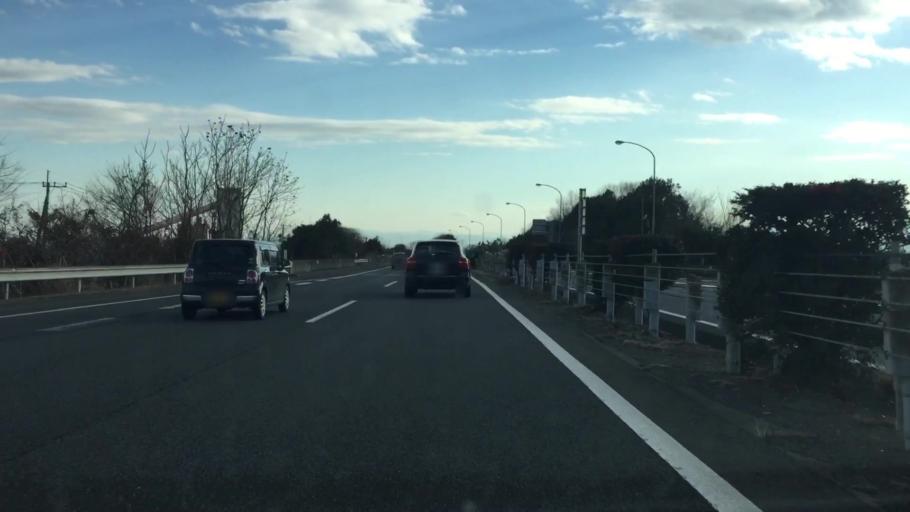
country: JP
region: Gunma
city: Kanekomachi
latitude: 36.4284
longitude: 139.0157
